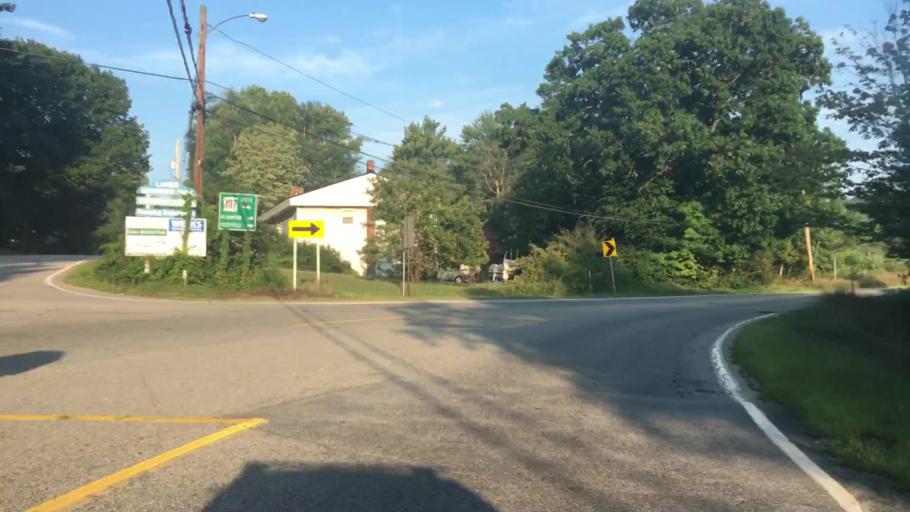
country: US
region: New Hampshire
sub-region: Belknap County
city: Laconia
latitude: 43.5144
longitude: -71.4565
